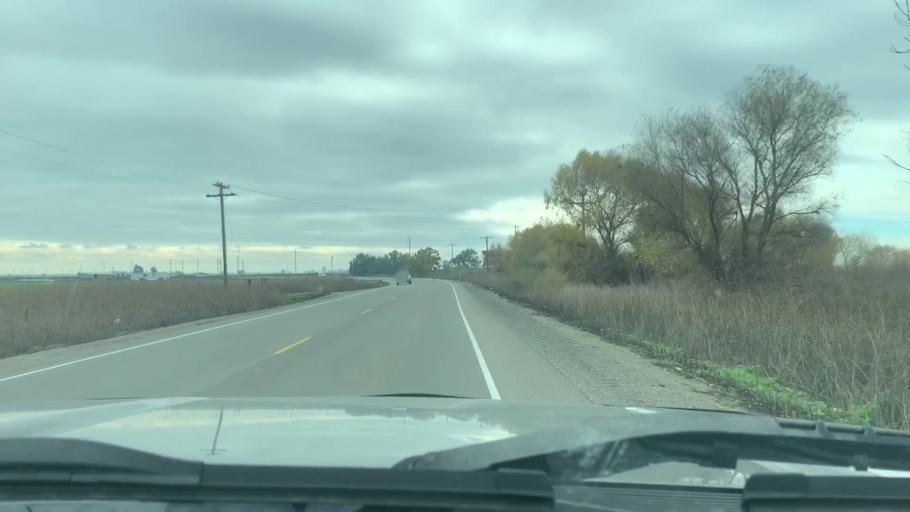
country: US
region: California
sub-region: Merced County
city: Los Banos
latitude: 37.1365
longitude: -120.8331
